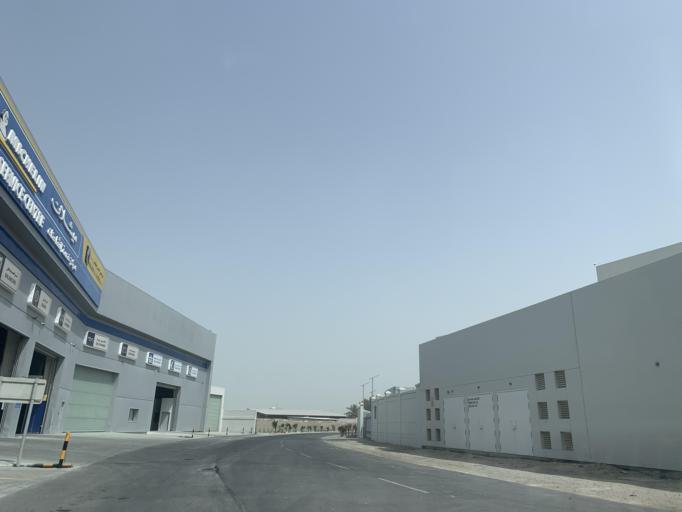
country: BH
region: Northern
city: Madinat `Isa
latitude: 26.1885
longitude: 50.5309
